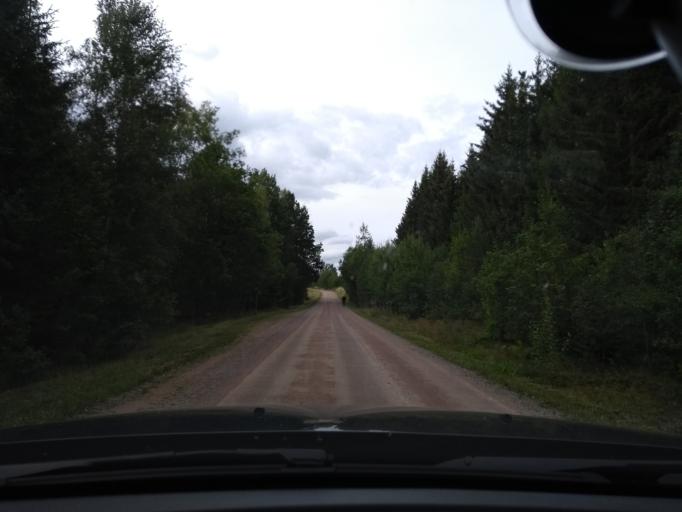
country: SE
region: Joenkoeping
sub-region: Eksjo Kommun
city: Mariannelund
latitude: 57.6292
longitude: 15.6391
